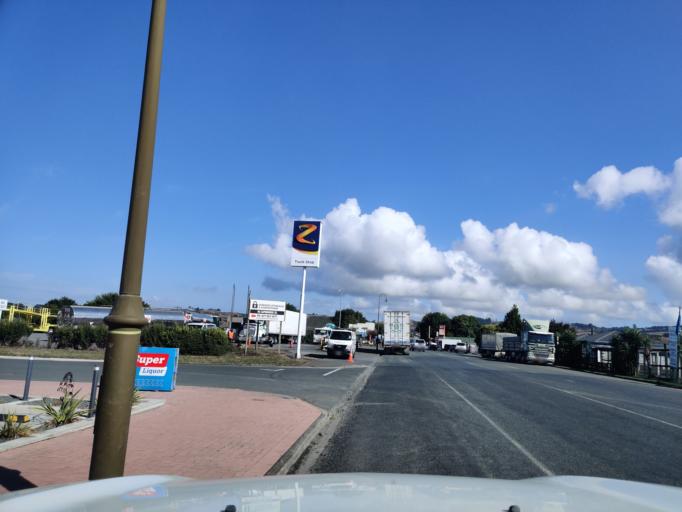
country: NZ
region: Auckland
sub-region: Auckland
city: Pukekohe East
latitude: -37.2467
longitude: 175.0235
